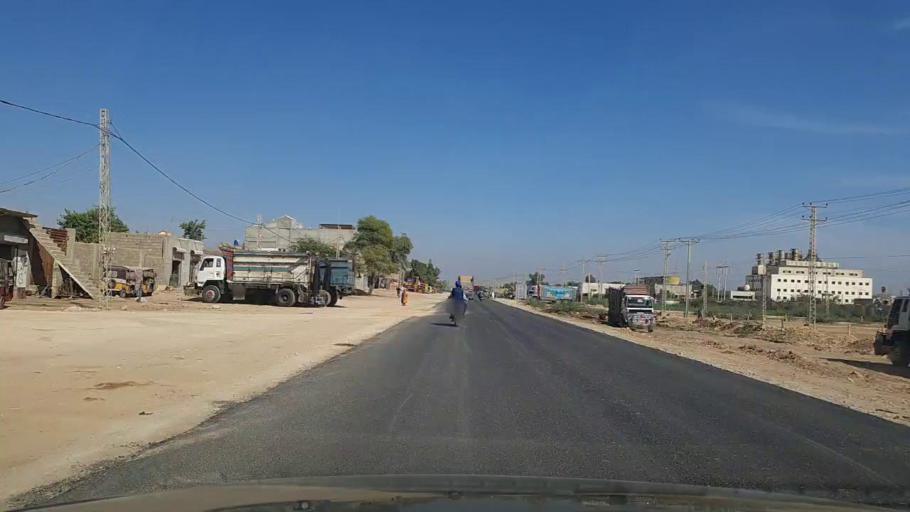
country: PK
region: Sindh
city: Kotri
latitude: 25.3398
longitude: 68.2513
